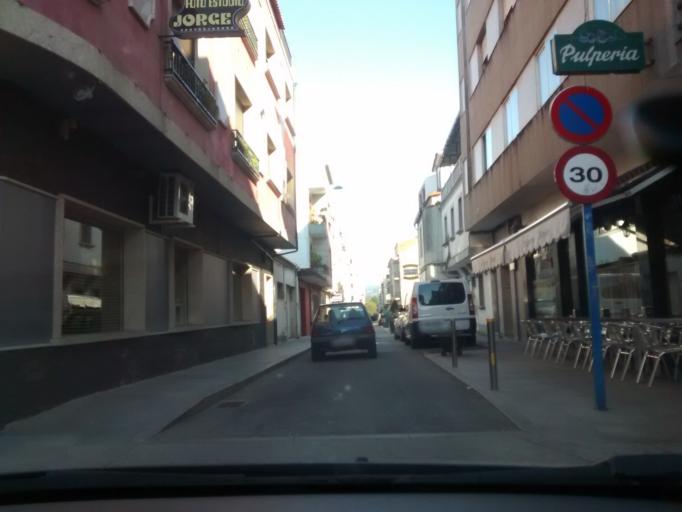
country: ES
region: Galicia
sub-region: Provincia de Pontevedra
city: O Grove
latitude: 42.4942
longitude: -8.8637
